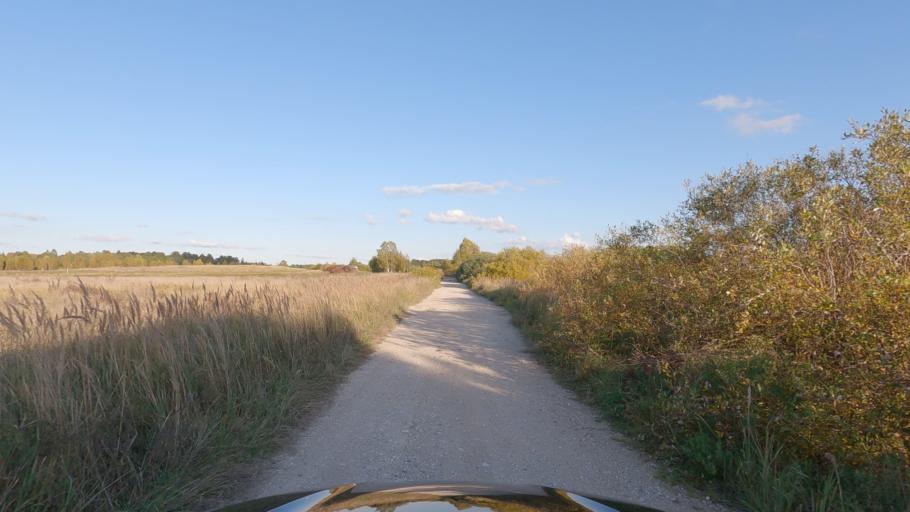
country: EE
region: Harju
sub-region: Saku vald
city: Saku
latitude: 59.2874
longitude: 24.7264
